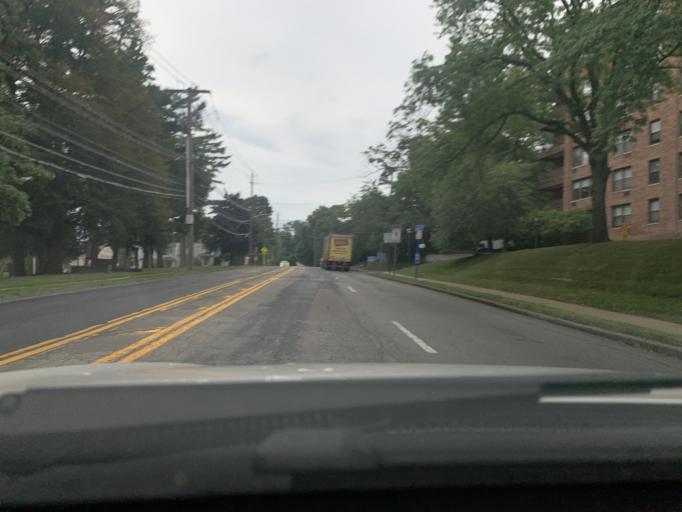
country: US
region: New York
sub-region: Westchester County
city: Ossining
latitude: 41.1522
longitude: -73.8597
